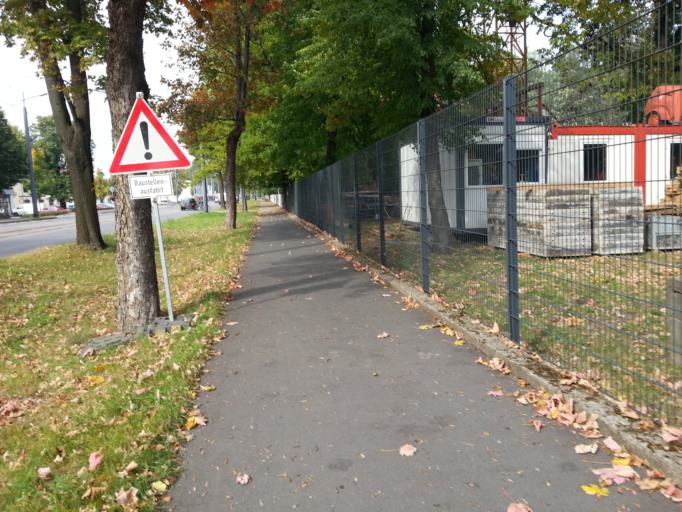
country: DE
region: Saxony
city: Radebeul
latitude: 51.0975
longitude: 13.6925
